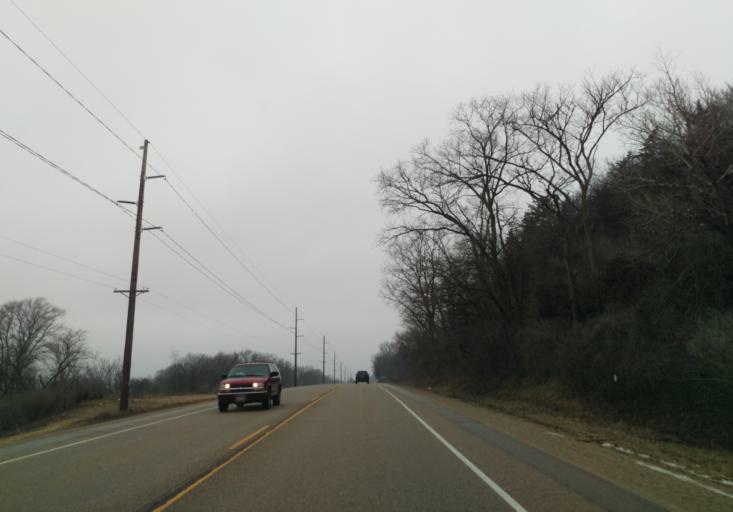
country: US
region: Wisconsin
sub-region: Dane County
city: Black Earth
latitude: 43.1299
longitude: -89.7185
